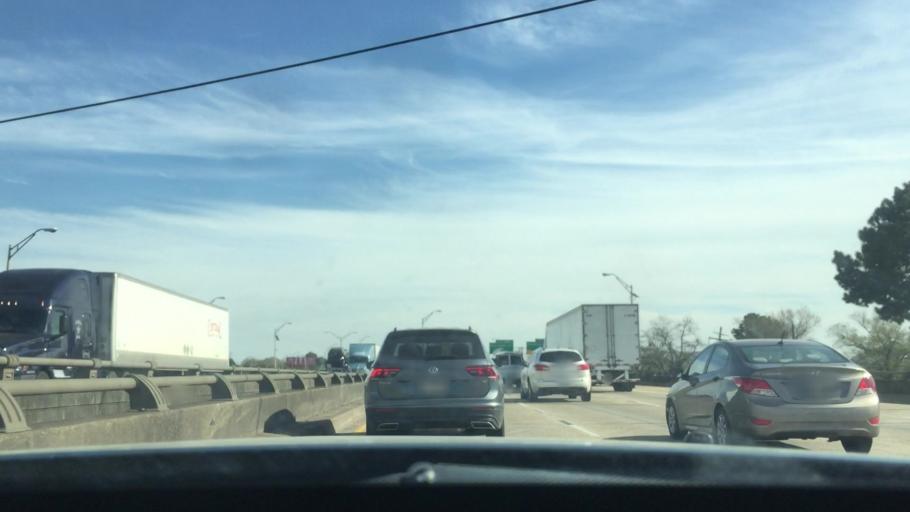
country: US
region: Louisiana
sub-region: East Baton Rouge Parish
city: Baton Rouge
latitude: 30.4344
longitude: -91.1769
